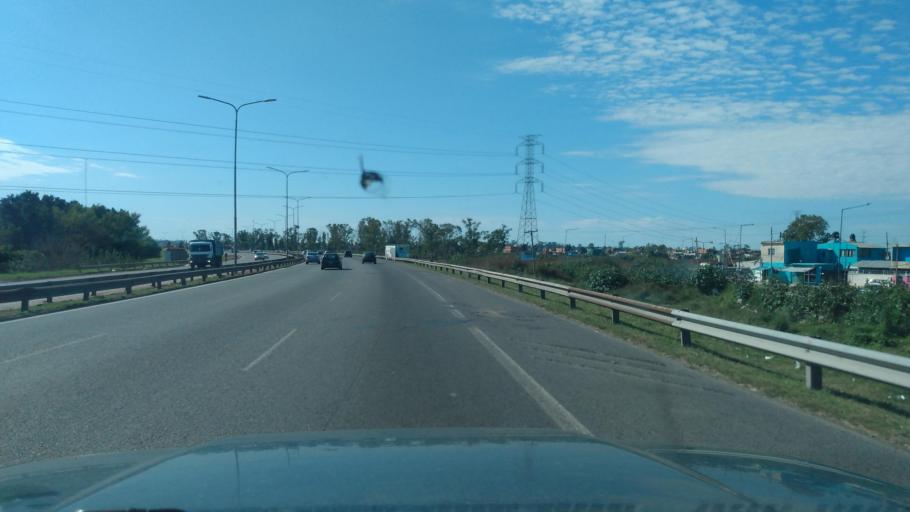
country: AR
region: Buenos Aires
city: Hurlingham
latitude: -34.5510
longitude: -58.6093
